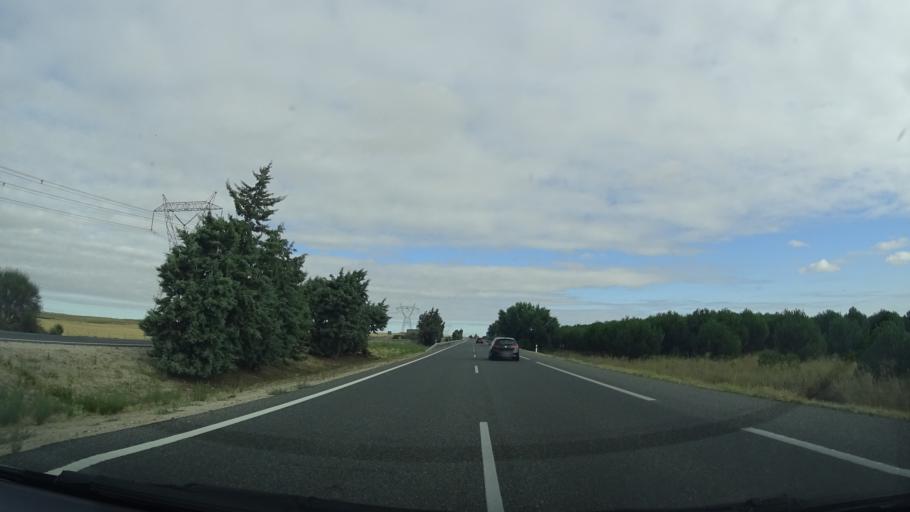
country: ES
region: Castille and Leon
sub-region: Provincia de Valladolid
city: San Pablo de la Moraleja
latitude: 41.1546
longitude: -4.7929
